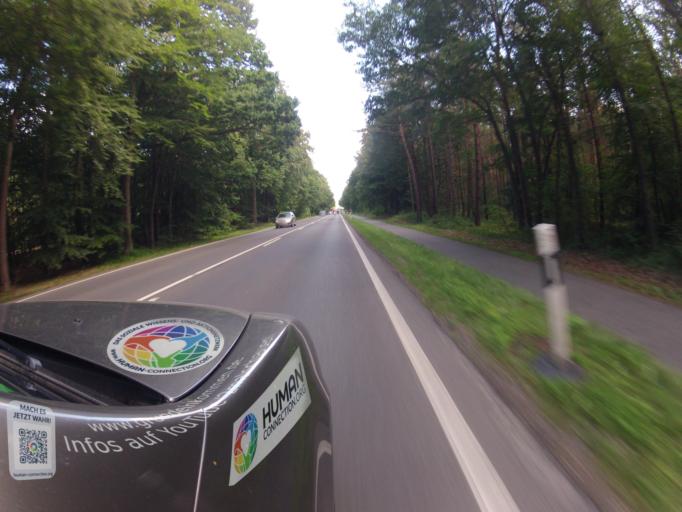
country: DE
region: Mecklenburg-Vorpommern
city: Loddin
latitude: 54.0254
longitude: 14.0348
